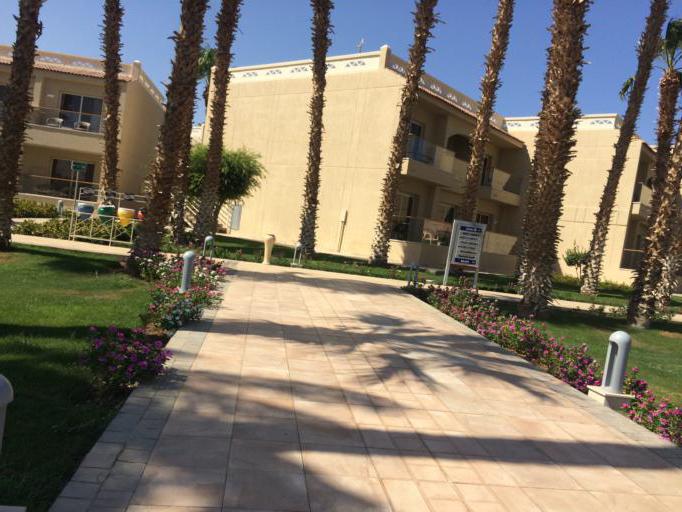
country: EG
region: Red Sea
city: Hurghada
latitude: 27.1224
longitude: 33.8263
